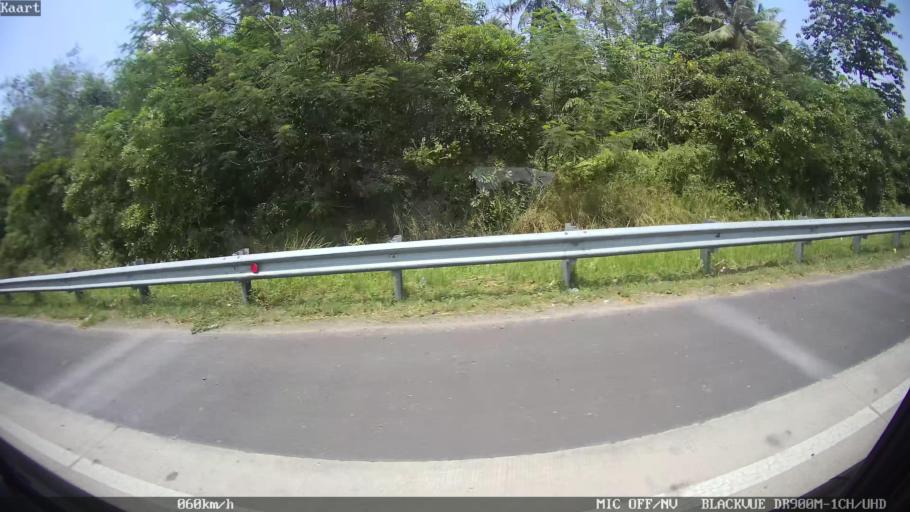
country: ID
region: Lampung
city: Kedaton
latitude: -5.3880
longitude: 105.3402
